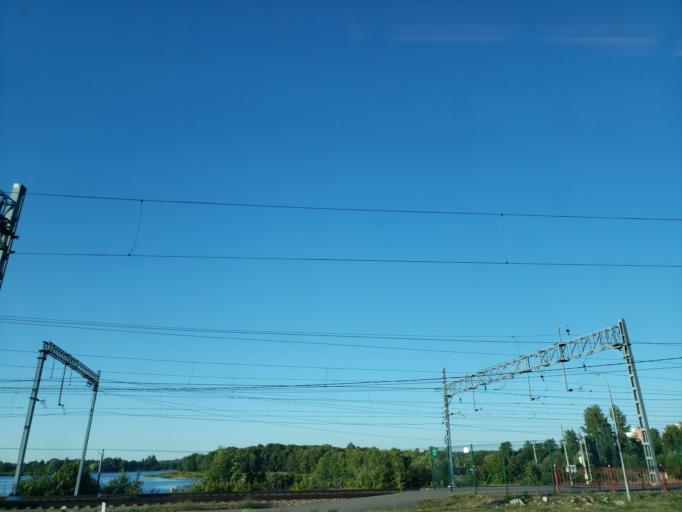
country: RU
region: Leningrad
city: Vyborg
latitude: 60.7162
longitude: 28.7468
